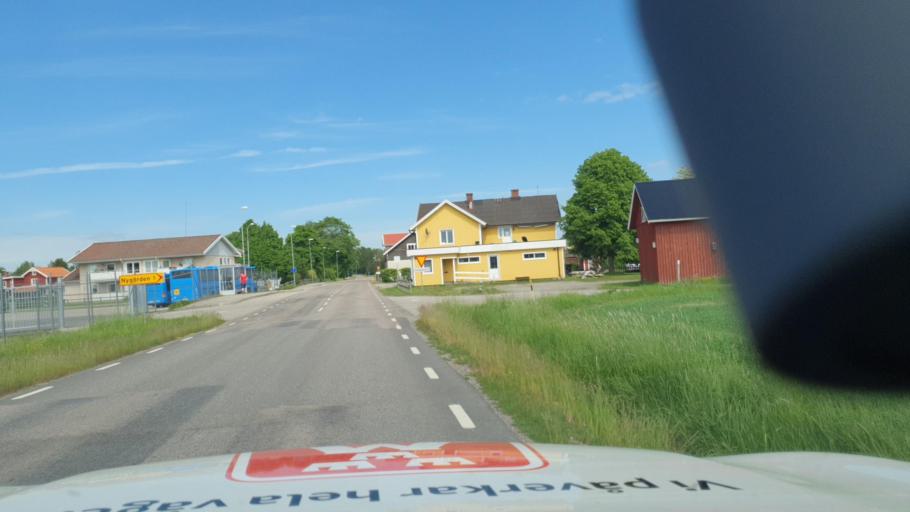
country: SE
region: Vaestra Goetaland
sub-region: Essunga Kommun
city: Nossebro
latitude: 58.2308
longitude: 12.6622
